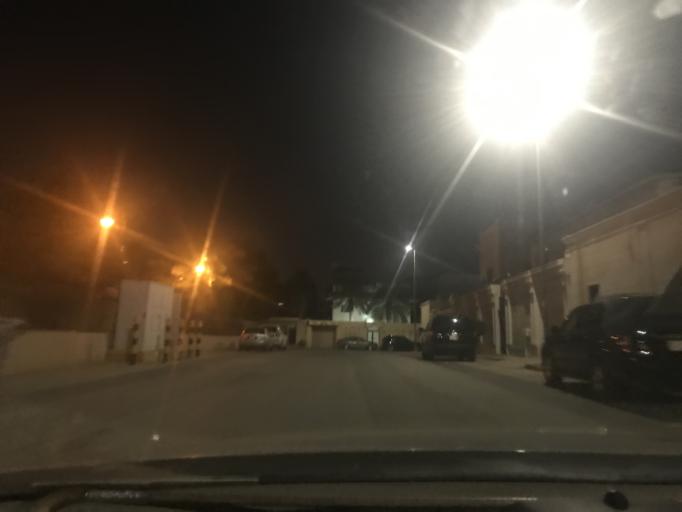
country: SA
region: Ar Riyad
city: Riyadh
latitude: 24.7395
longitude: 46.7620
